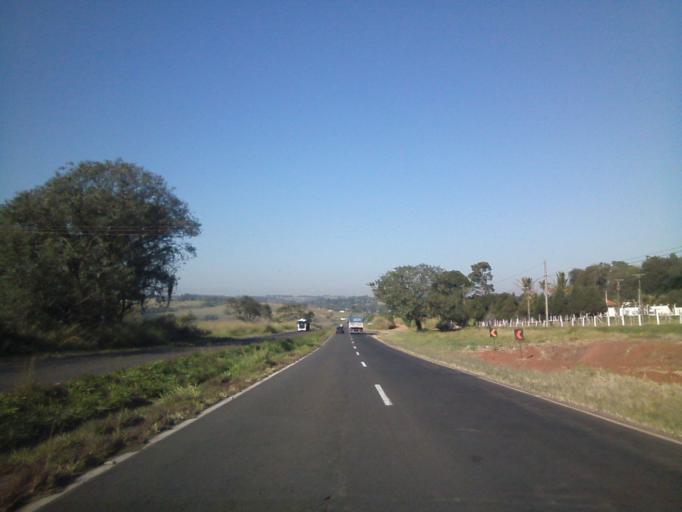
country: BR
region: Sao Paulo
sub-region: Presidente Prudente
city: Presidente Prudente
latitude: -22.1960
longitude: -51.4333
